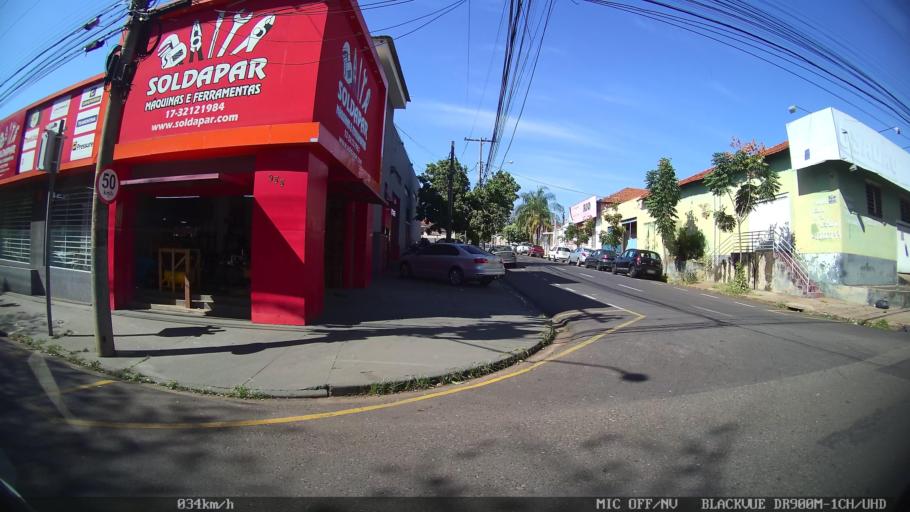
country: BR
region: Sao Paulo
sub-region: Sao Jose Do Rio Preto
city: Sao Jose do Rio Preto
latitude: -20.7987
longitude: -49.3943
